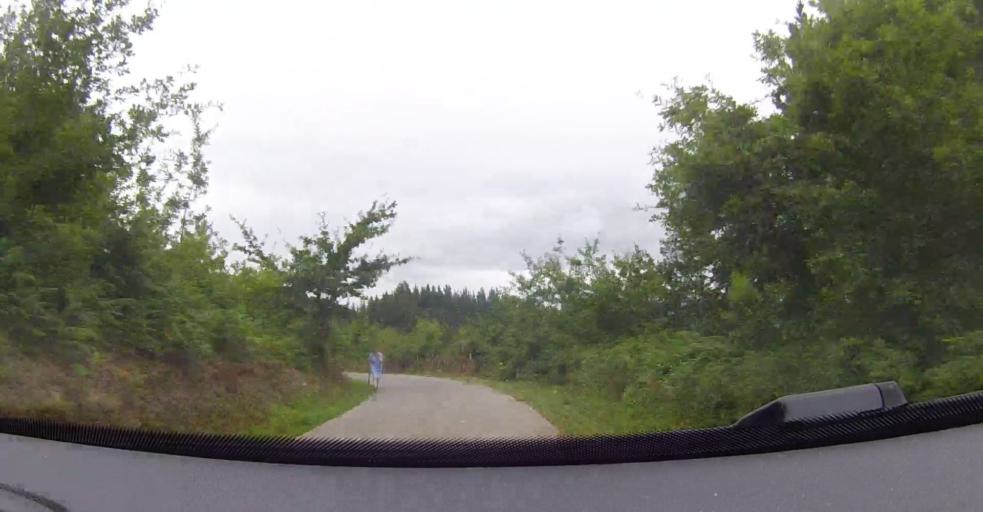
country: ES
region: Basque Country
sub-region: Bizkaia
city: Urrestieta
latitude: 43.2296
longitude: -3.1749
